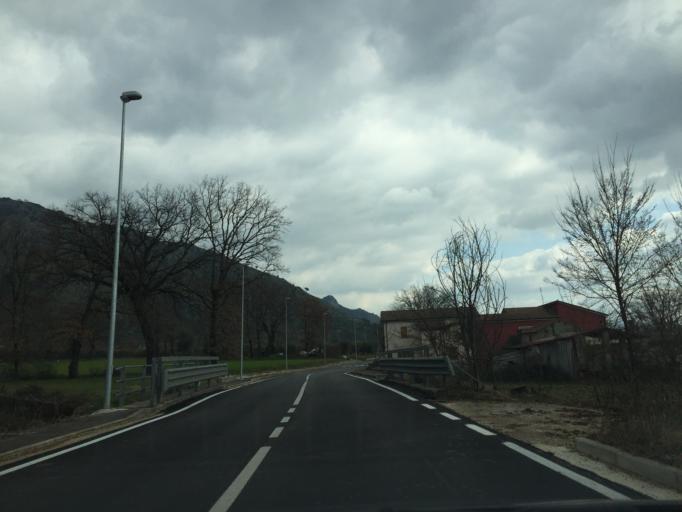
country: IT
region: Latium
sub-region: Provincia di Frosinone
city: Villa Santa Lucia
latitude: 41.4956
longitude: 13.7705
